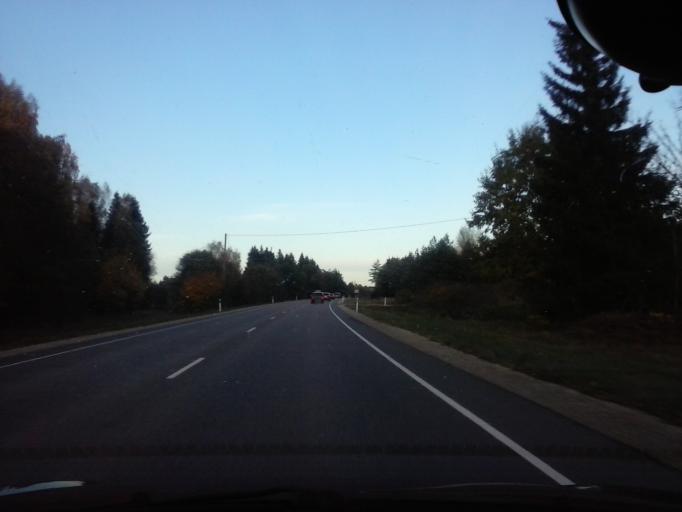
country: EE
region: Harju
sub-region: Nissi vald
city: Turba
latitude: 58.9906
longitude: 24.0226
